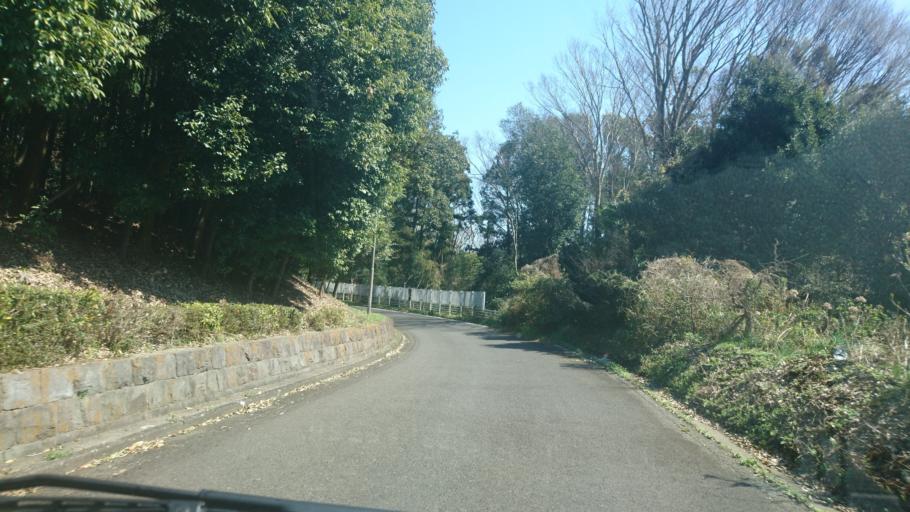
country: JP
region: Kanagawa
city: Fujisawa
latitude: 35.3862
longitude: 139.4296
